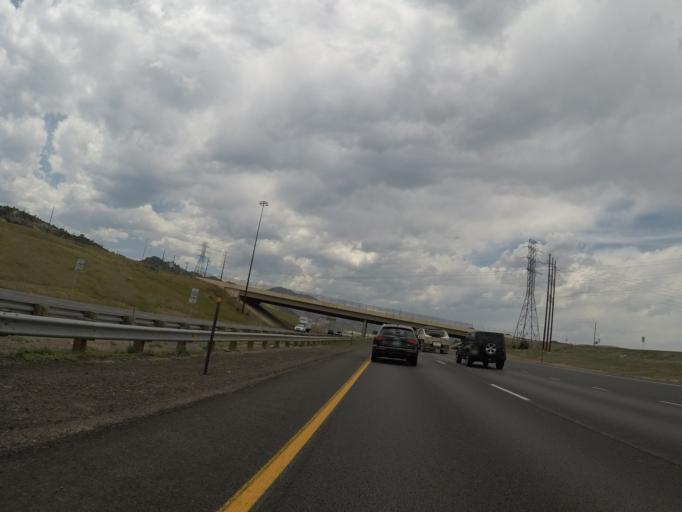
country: US
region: Colorado
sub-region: Jefferson County
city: Ken Caryl
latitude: 39.6311
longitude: -105.1594
